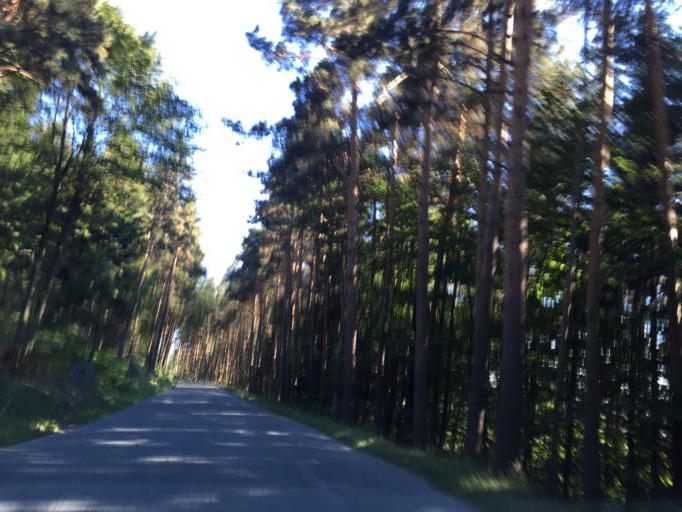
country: FR
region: Rhone-Alpes
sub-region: Departement de la Loire
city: Saint-Julien-Molin-Molette
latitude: 45.3435
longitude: 4.5745
